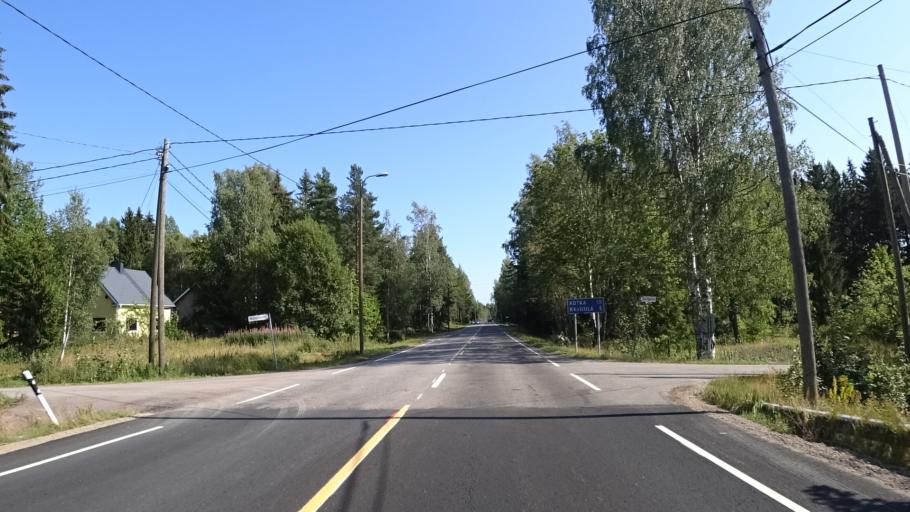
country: FI
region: Kymenlaakso
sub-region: Kotka-Hamina
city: Karhula
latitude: 60.5463
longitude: 26.9168
